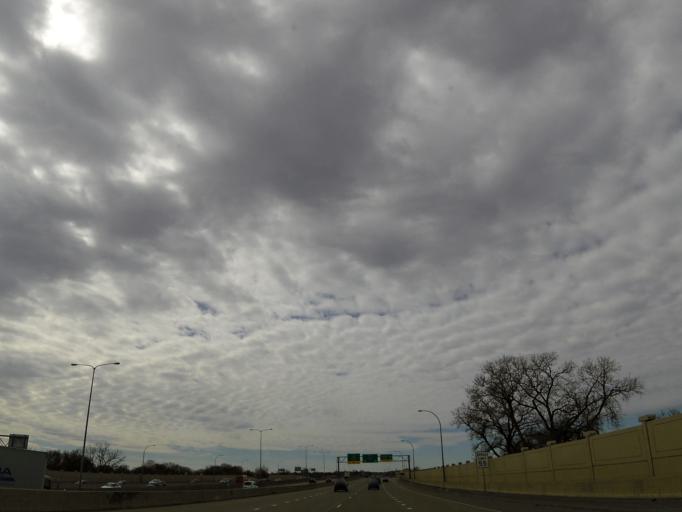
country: US
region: Minnesota
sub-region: Hennepin County
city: Richfield
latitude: 44.8904
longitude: -93.2802
